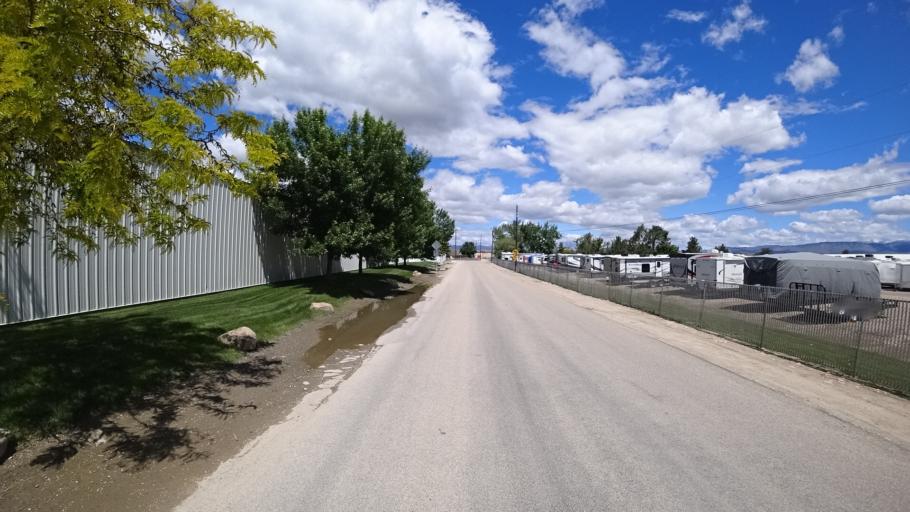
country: US
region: Idaho
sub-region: Ada County
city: Eagle
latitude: 43.6618
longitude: -116.3192
